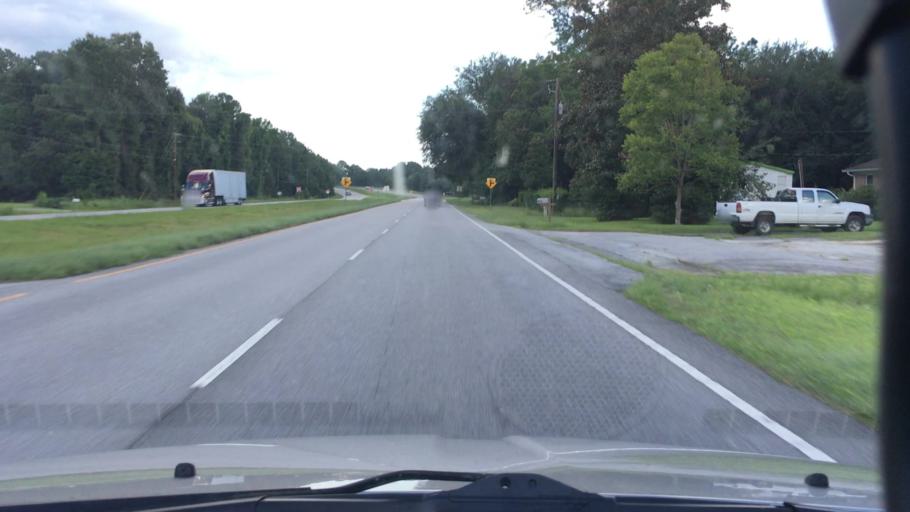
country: US
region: South Carolina
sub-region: Hampton County
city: Yemassee
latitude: 32.6041
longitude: -80.8031
